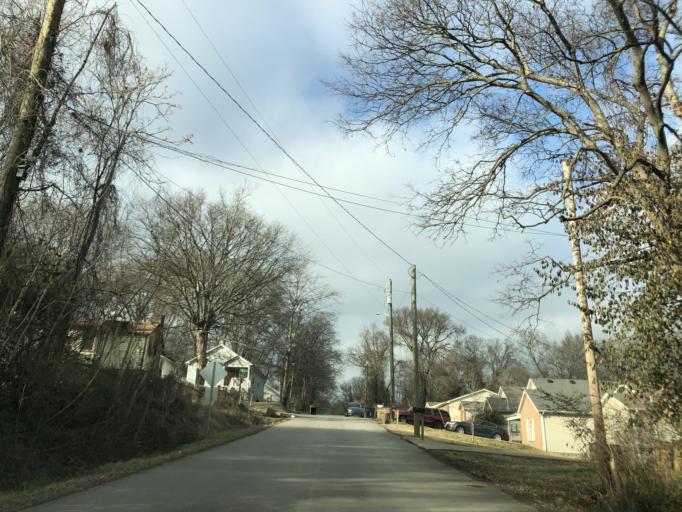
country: US
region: Tennessee
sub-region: Davidson County
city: Nashville
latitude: 36.2032
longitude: -86.7831
